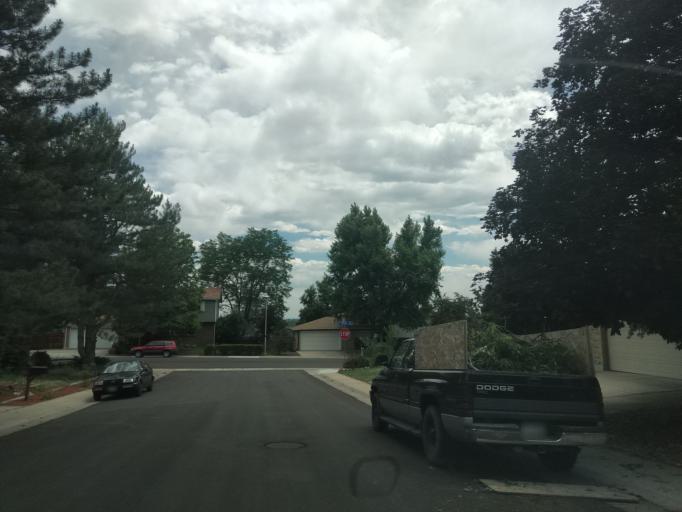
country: US
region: Colorado
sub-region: Jefferson County
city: Lakewood
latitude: 39.6730
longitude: -105.0986
